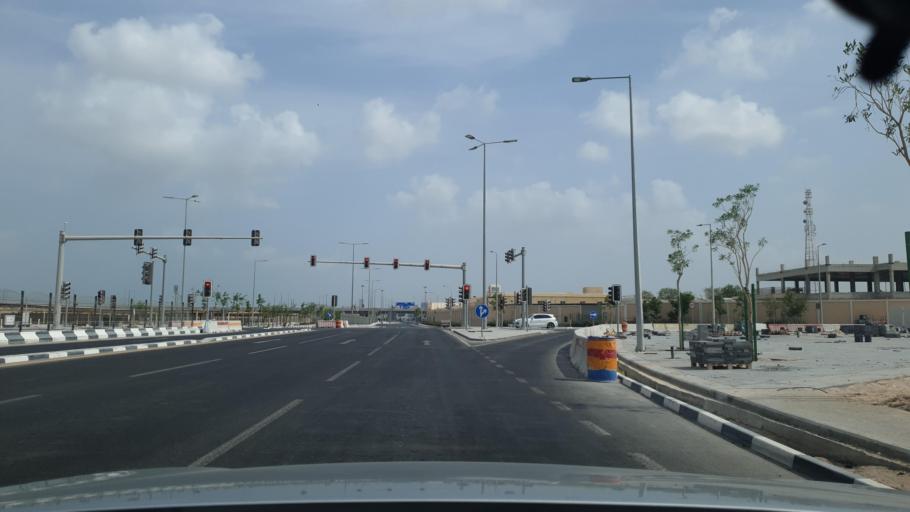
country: QA
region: Baladiyat ar Rayyan
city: Ar Rayyan
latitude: 25.2781
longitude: 51.4661
